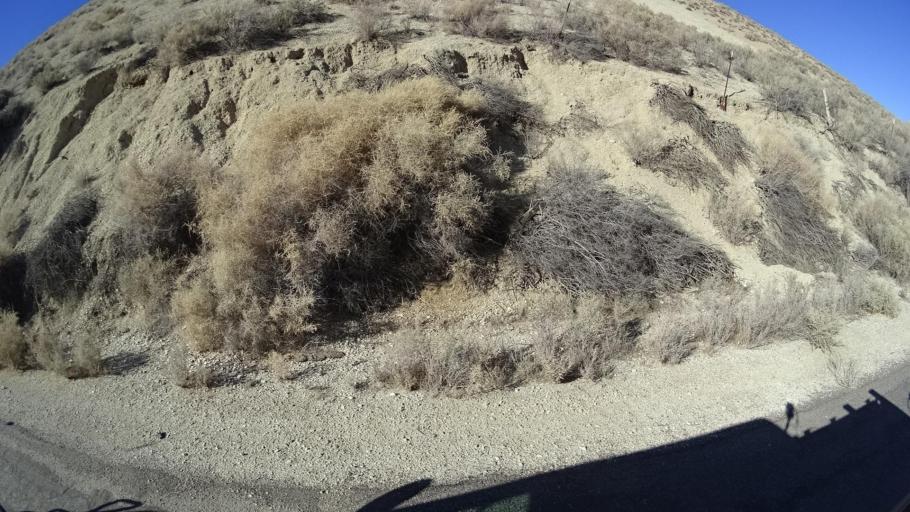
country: US
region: California
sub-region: Kern County
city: Maricopa
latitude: 34.9786
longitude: -119.4054
